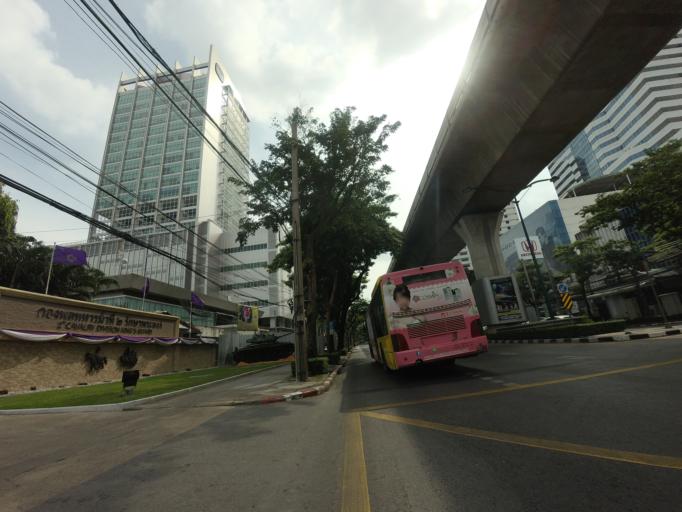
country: TH
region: Bangkok
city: Phaya Thai
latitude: 13.7715
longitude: 100.5421
